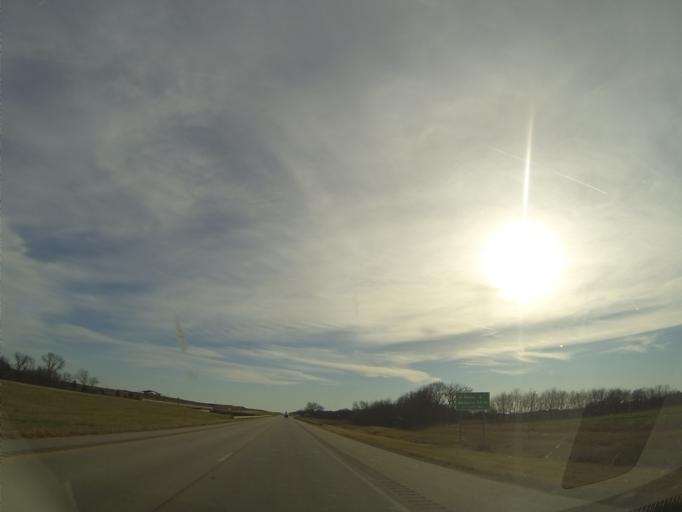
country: US
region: Kansas
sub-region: Ottawa County
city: Minneapolis
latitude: 39.1367
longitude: -97.6692
